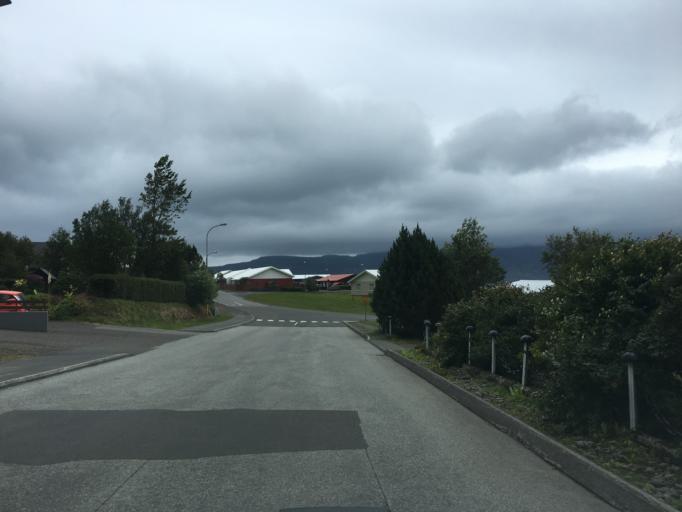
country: IS
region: East
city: Neskaupstadur
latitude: 65.1485
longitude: -13.6730
